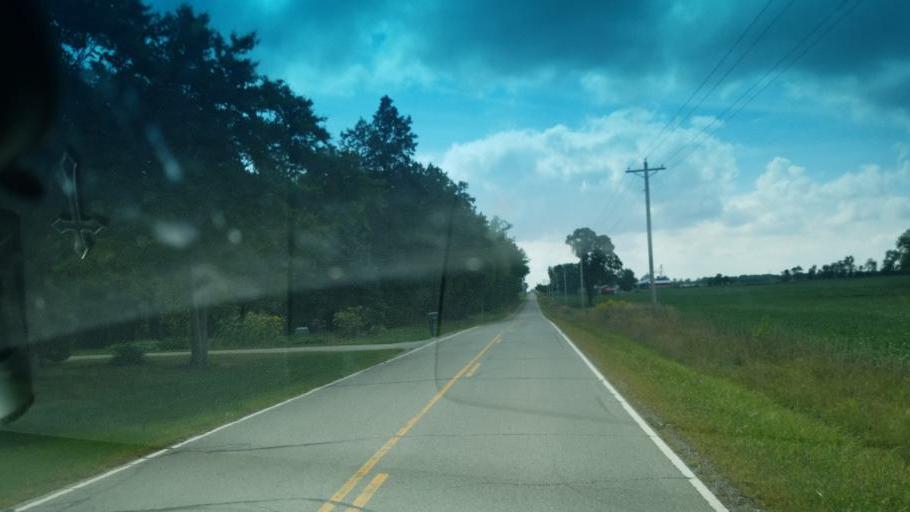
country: US
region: Ohio
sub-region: Crawford County
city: Bucyrus
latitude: 40.9635
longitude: -82.9016
